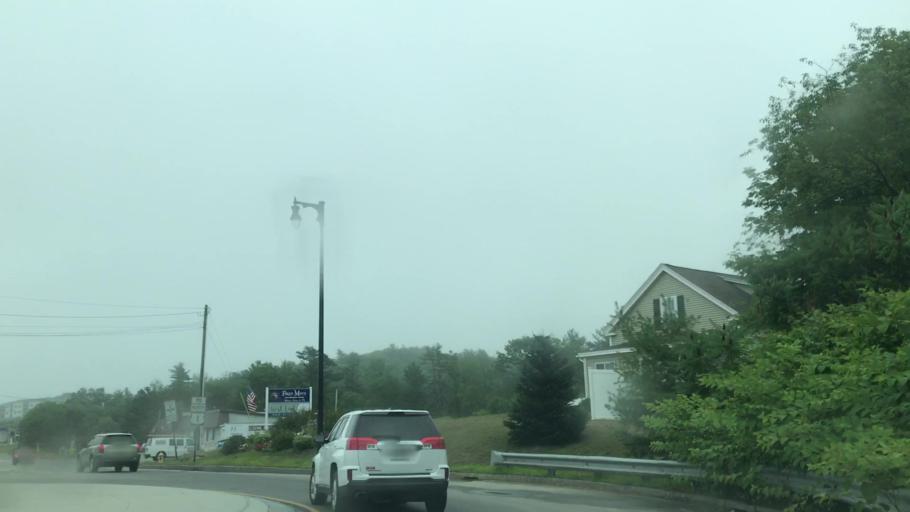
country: US
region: Maine
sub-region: Sagadahoc County
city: Bath
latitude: 43.9057
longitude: -69.8327
